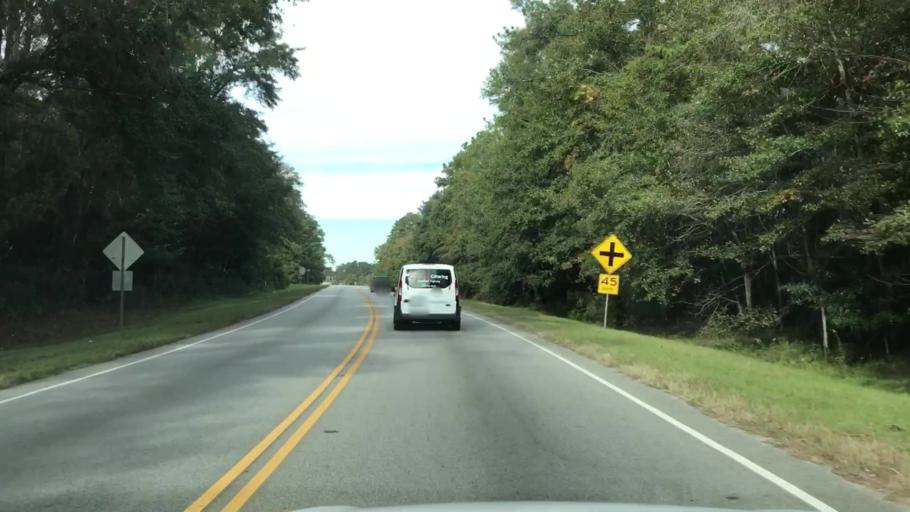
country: US
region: South Carolina
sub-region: Colleton County
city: Walterboro
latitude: 32.9108
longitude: -80.6433
